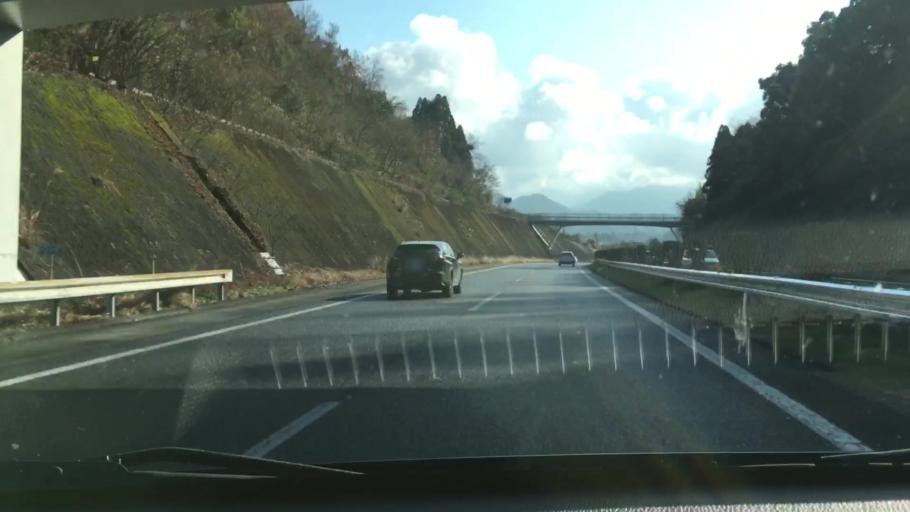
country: JP
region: Kumamoto
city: Matsubase
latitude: 32.5888
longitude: 130.7164
